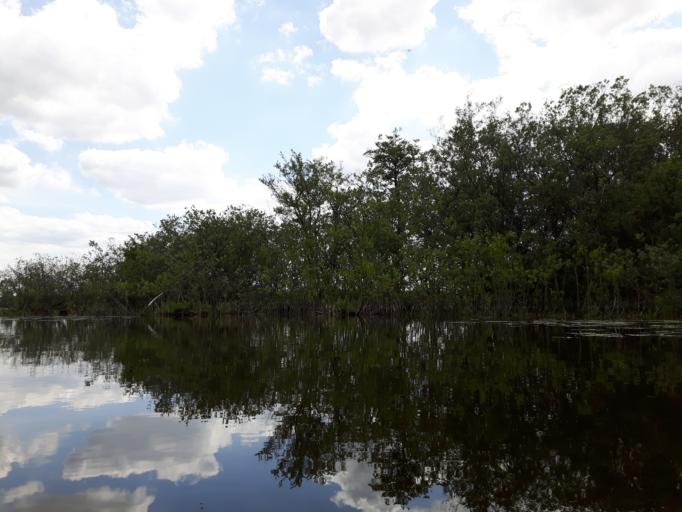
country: DE
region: Schleswig-Holstein
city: Muhbrook
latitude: 54.1420
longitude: 9.9972
